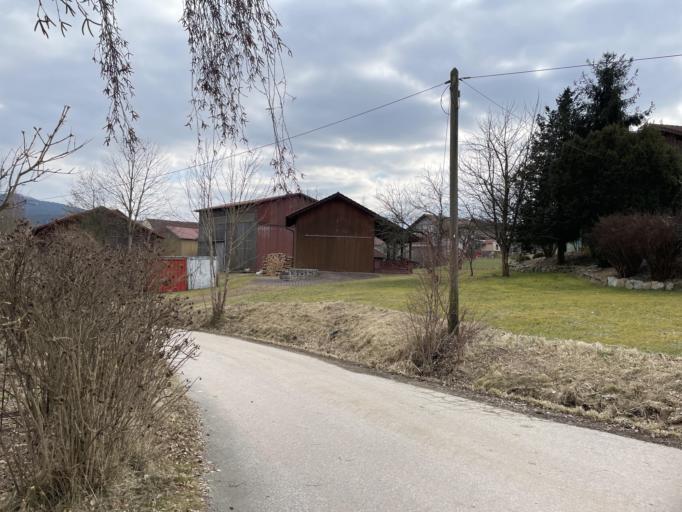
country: DE
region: Bavaria
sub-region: Upper Palatinate
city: Runding
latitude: 49.2249
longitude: 12.7618
